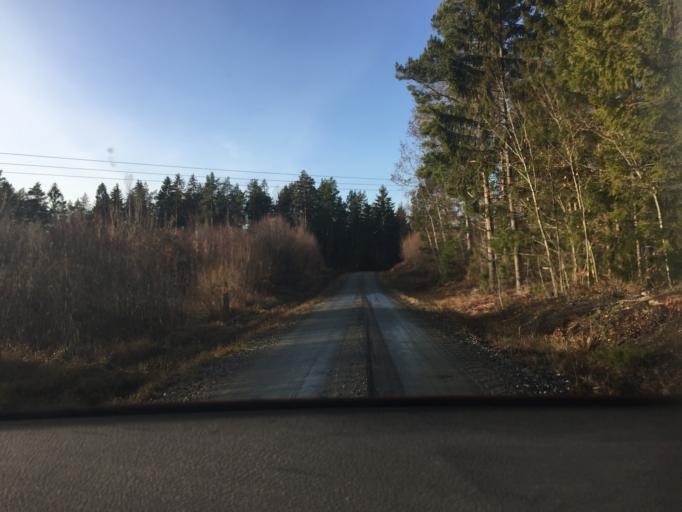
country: SE
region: Soedermanland
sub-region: Nykopings Kommun
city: Olstorp
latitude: 58.6214
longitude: 16.5964
